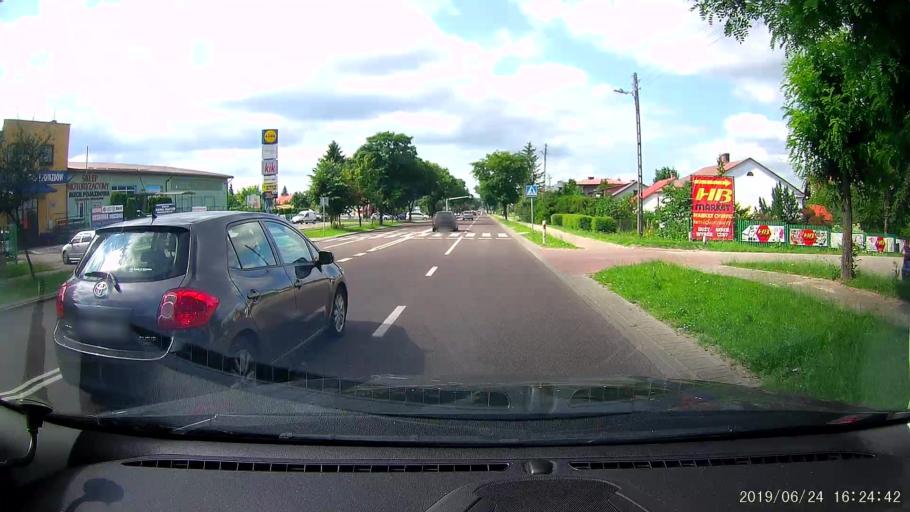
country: PL
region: Lublin Voivodeship
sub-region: Powiat tomaszowski
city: Tomaszow Lubelski
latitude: 50.4374
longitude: 23.4196
